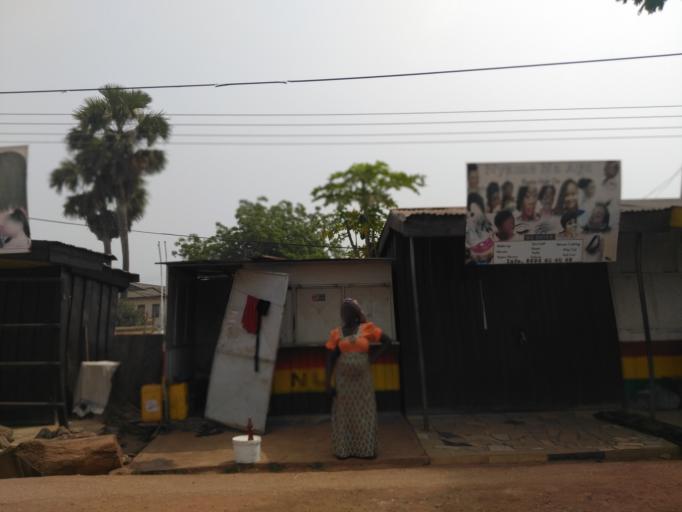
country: GH
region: Ashanti
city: Kumasi
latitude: 6.7075
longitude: -1.6385
